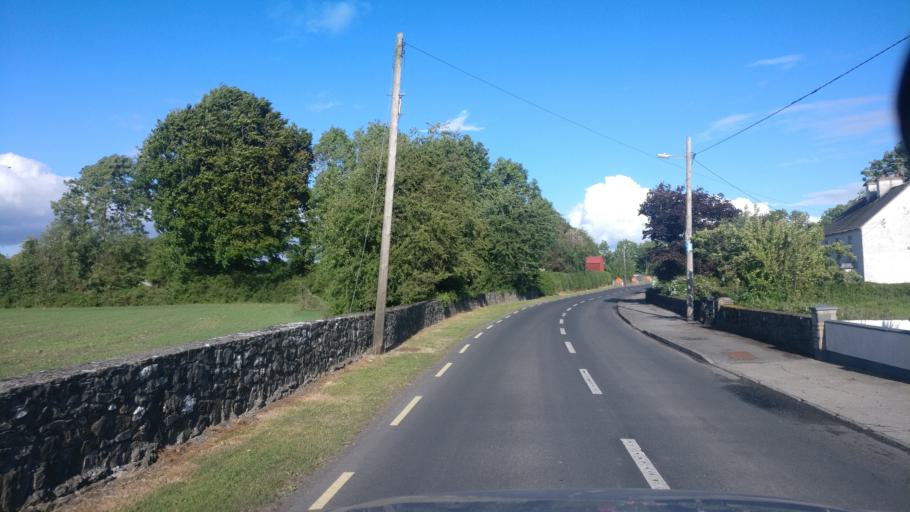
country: IE
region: Connaught
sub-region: County Galway
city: Ballinasloe
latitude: 53.2352
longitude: -8.2674
